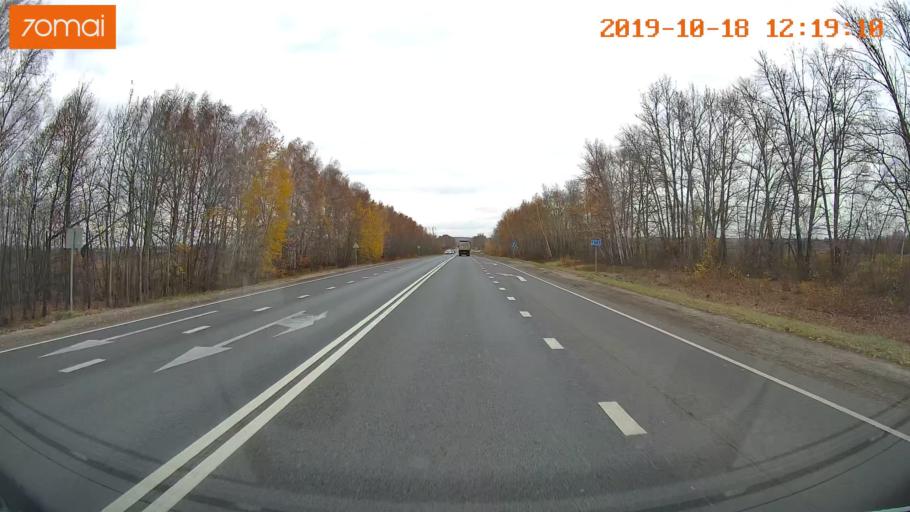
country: RU
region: Rjazan
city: Zakharovo
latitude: 54.4784
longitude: 39.4650
